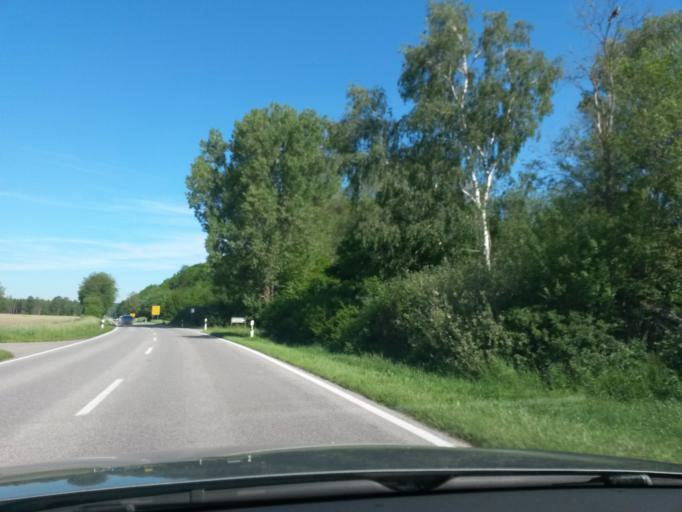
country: DE
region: Baden-Wuerttemberg
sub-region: Tuebingen Region
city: Durnau
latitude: 48.0648
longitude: 9.5784
